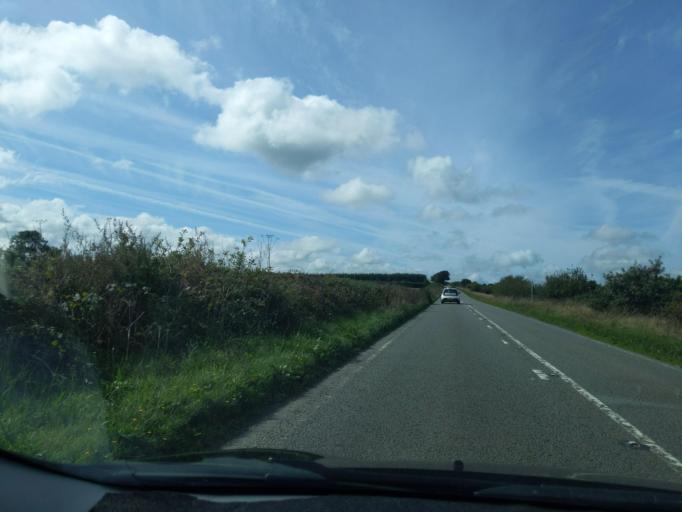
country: GB
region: England
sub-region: Cornwall
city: Trewen
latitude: 50.6332
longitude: -4.4838
